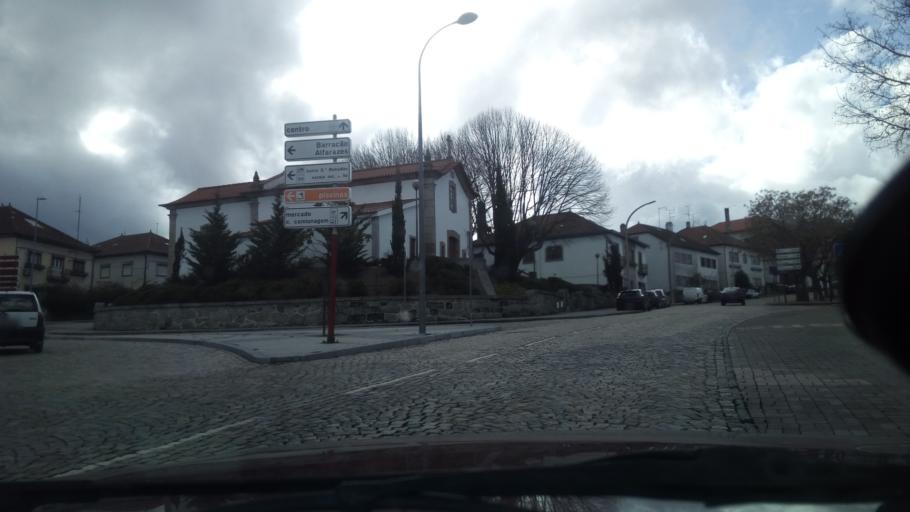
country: PT
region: Guarda
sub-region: Guarda
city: Guarda
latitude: 40.5340
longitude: -7.2634
